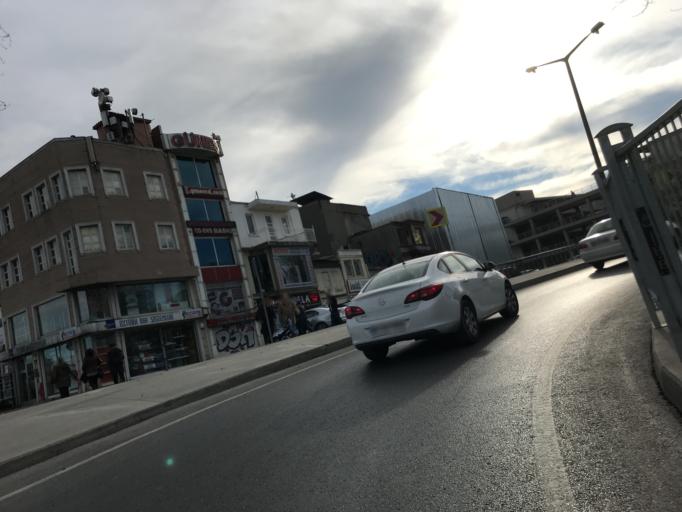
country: TR
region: Istanbul
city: Eminoenue
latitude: 41.0221
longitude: 28.9614
